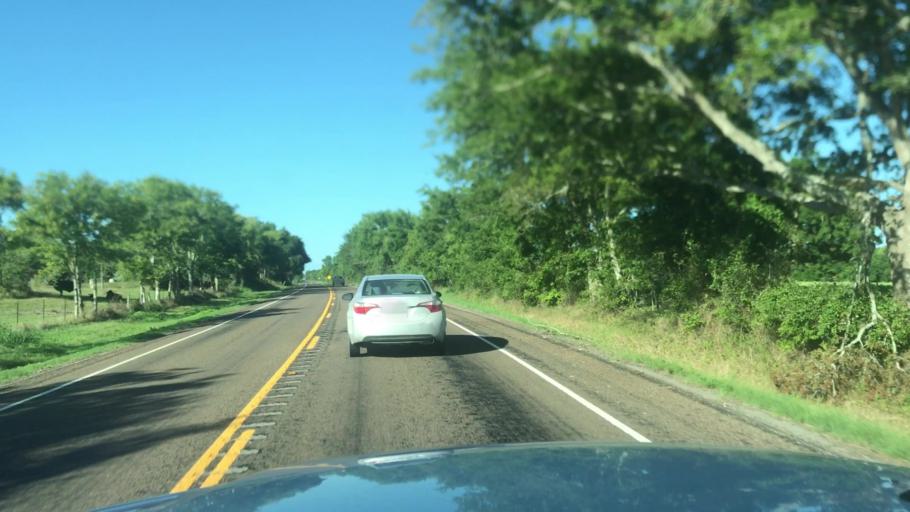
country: US
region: Texas
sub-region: Grimes County
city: Anderson
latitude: 30.6328
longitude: -95.8689
